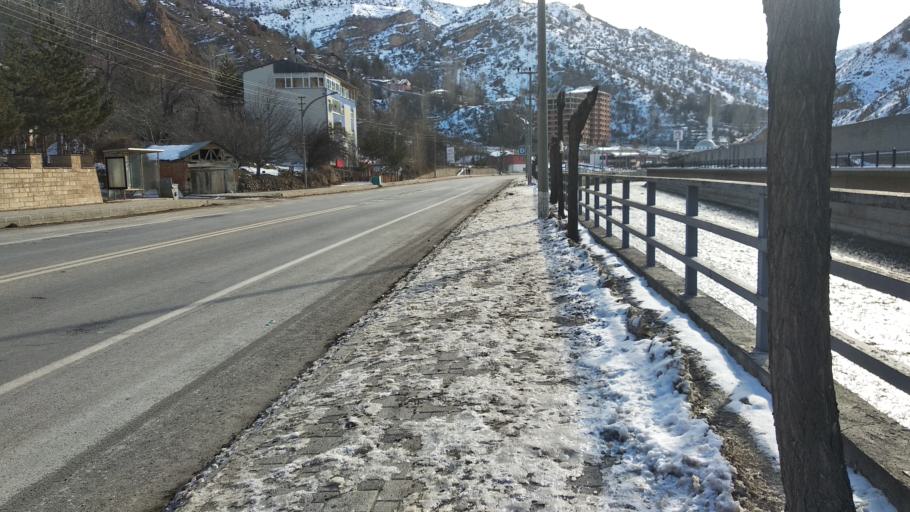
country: TR
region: Gumushane
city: Gumushkhane
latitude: 40.4471
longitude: 39.5013
